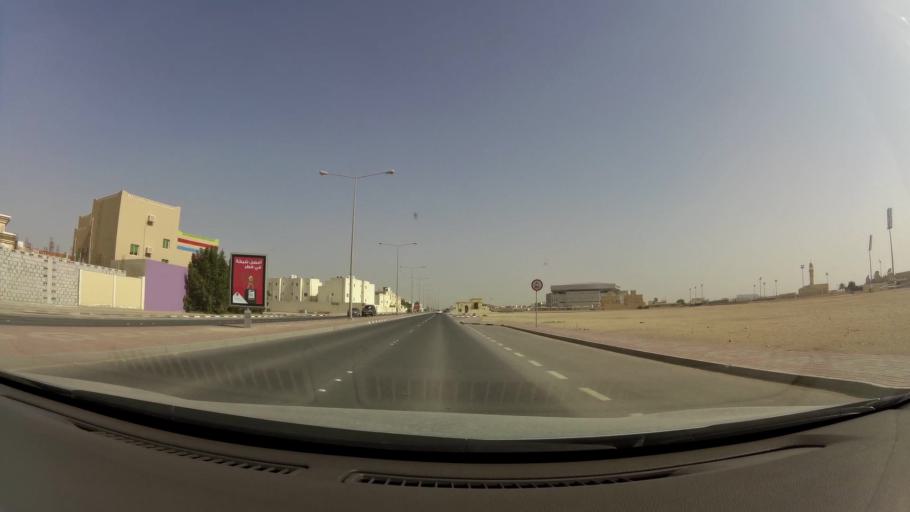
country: QA
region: Baladiyat ar Rayyan
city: Ar Rayyan
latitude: 25.3489
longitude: 51.4426
